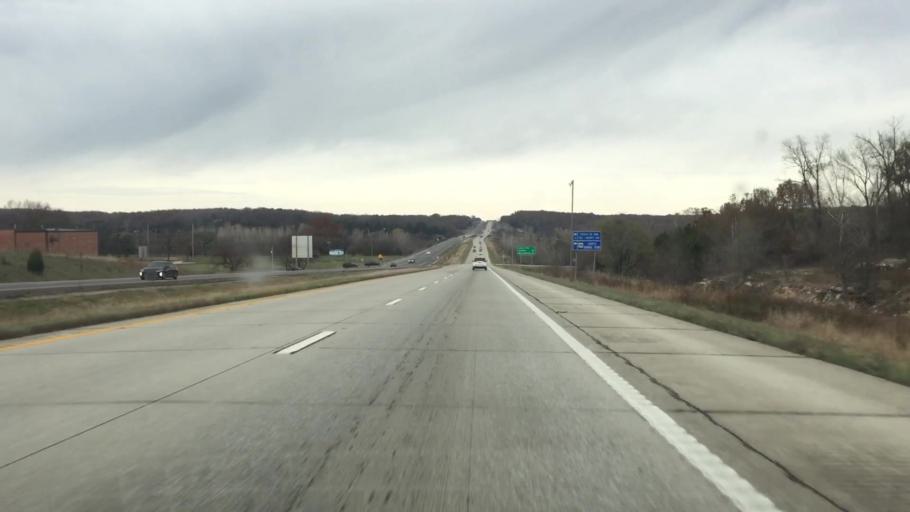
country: US
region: Missouri
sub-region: Saint Clair County
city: Osceola
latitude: 38.0512
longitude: -93.6874
